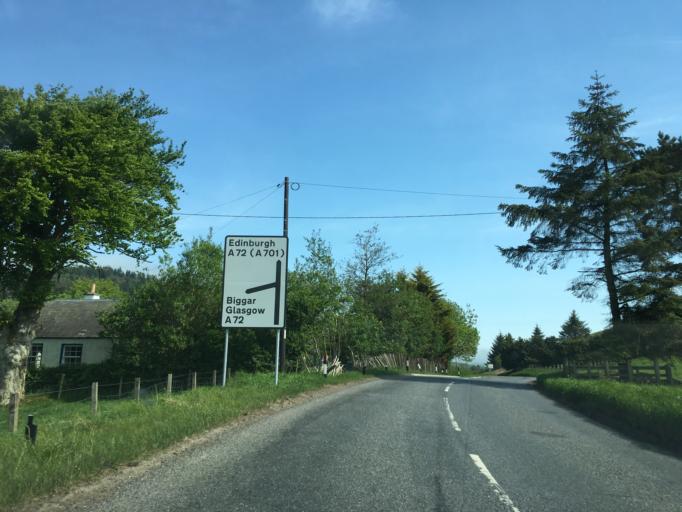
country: GB
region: Scotland
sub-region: South Lanarkshire
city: Biggar
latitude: 55.6529
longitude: -3.4341
